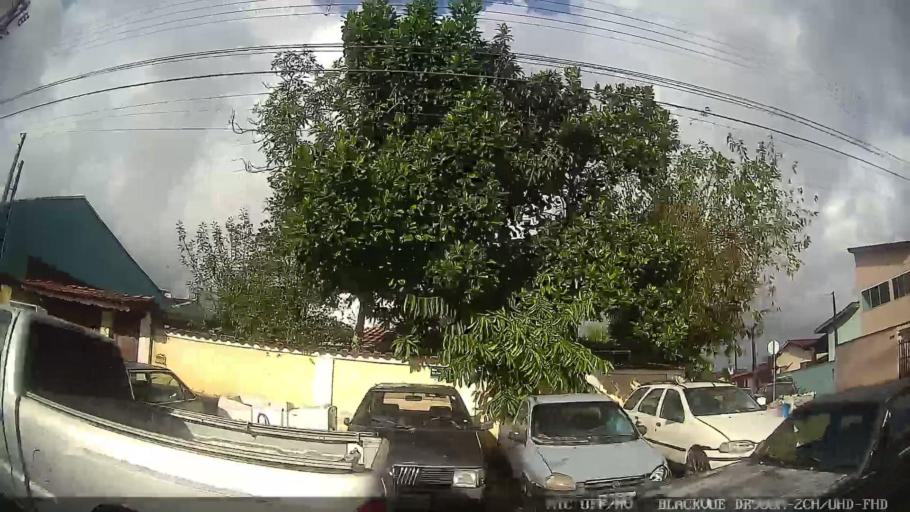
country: BR
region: Sao Paulo
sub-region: Itanhaem
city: Itanhaem
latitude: -24.2167
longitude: -46.8835
